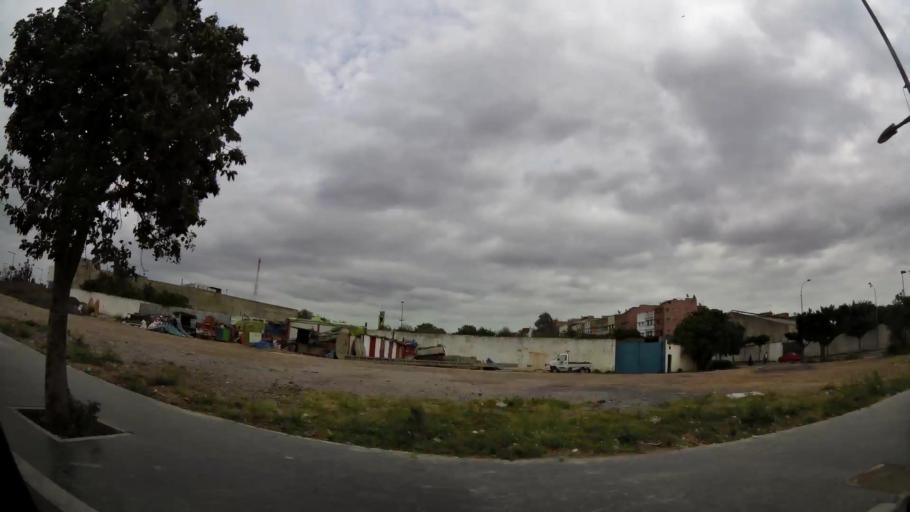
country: MA
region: Grand Casablanca
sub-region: Casablanca
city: Casablanca
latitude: 33.5745
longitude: -7.5777
